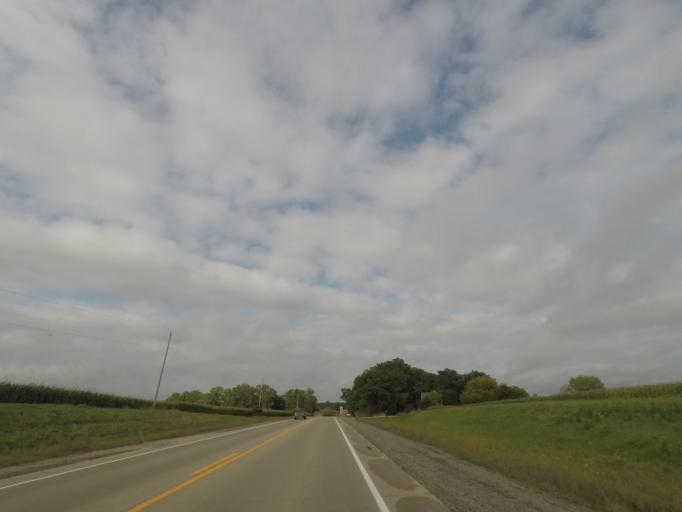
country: US
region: Wisconsin
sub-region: Dane County
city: Cottage Grove
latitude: 43.0289
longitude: -89.1652
